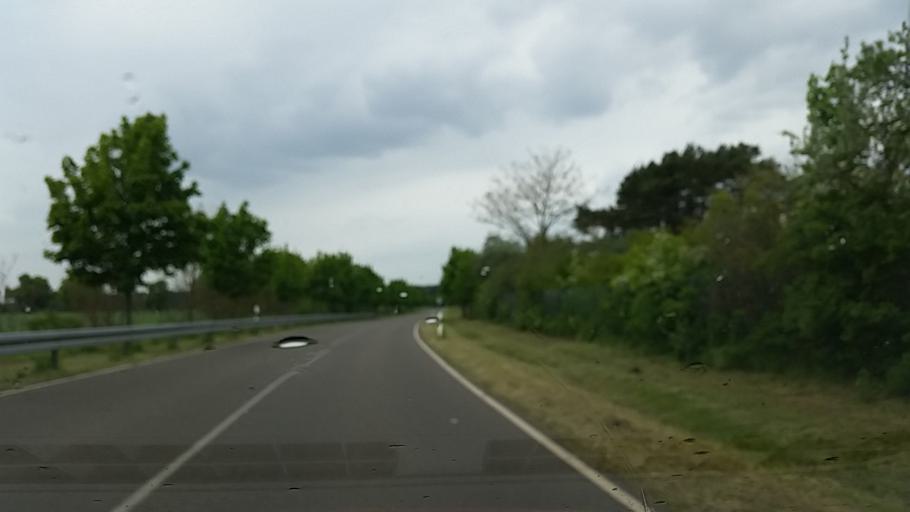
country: DE
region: Brandenburg
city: Rauen
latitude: 52.3195
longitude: 13.9529
